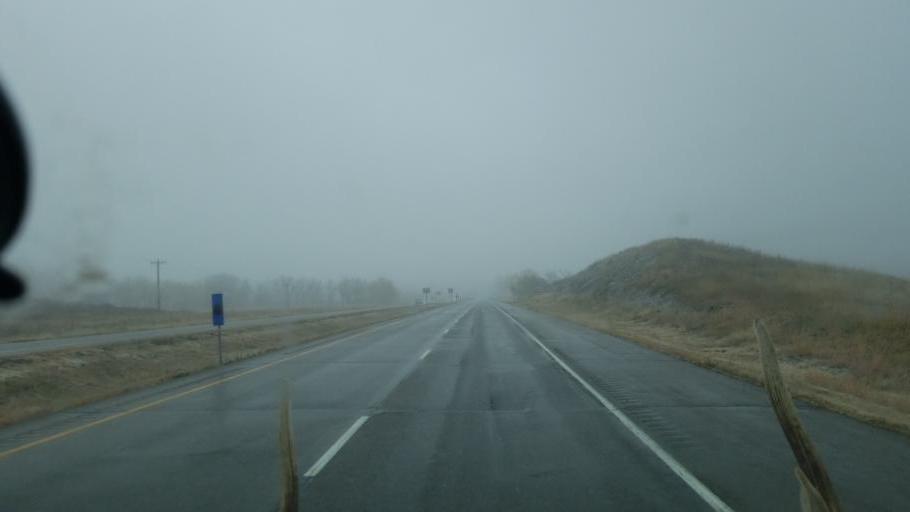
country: US
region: Colorado
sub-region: Pueblo County
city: Colorado City
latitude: 38.0192
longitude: -104.7398
